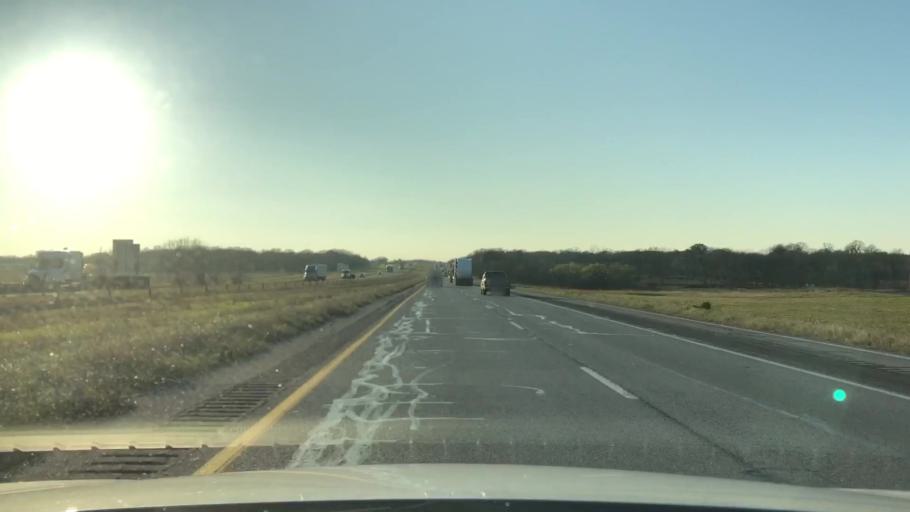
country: US
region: Texas
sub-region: Caldwell County
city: Luling
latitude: 29.6507
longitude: -97.6043
